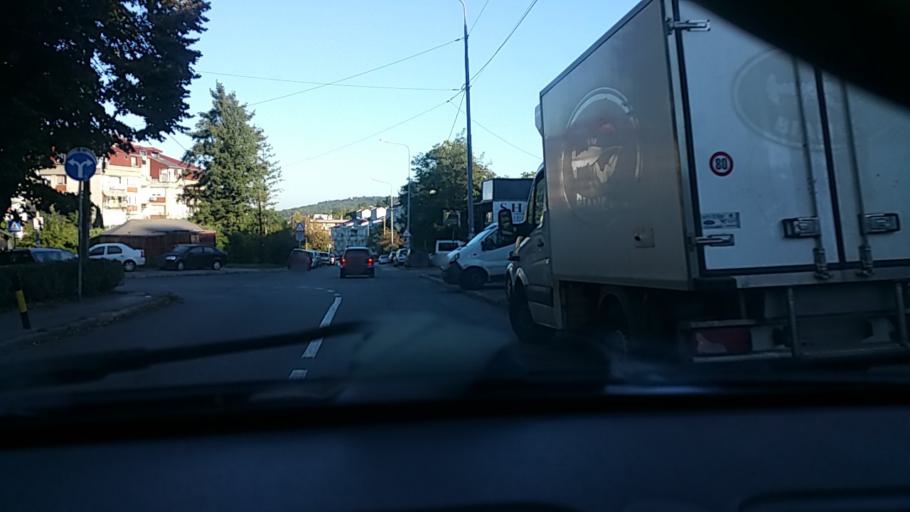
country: RS
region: Central Serbia
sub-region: Belgrade
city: Rakovica
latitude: 44.7479
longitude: 20.4609
